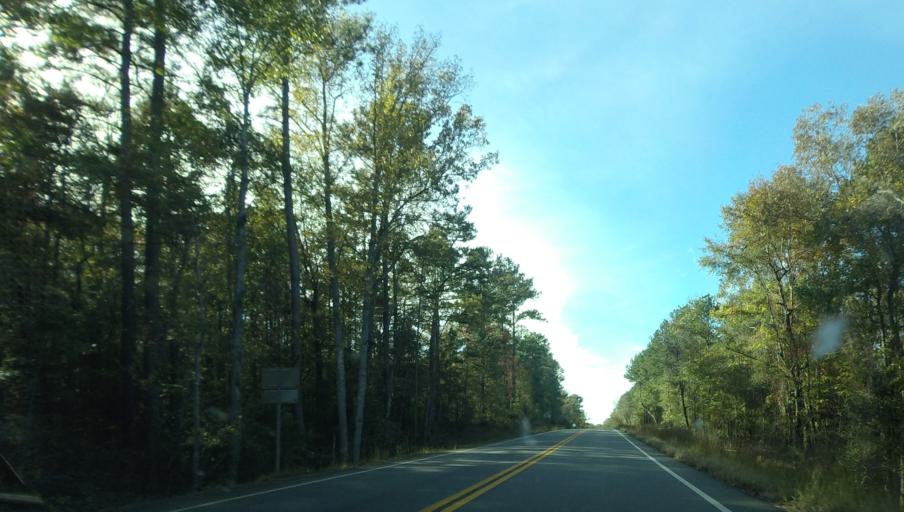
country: US
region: Georgia
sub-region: Taylor County
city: Butler
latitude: 32.7143
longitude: -84.2377
